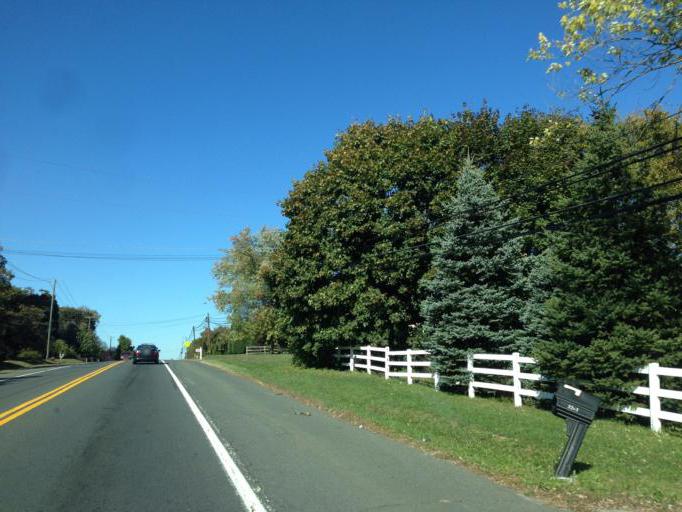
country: US
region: Maryland
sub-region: Montgomery County
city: Clarksburg
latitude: 39.2273
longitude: -77.2367
